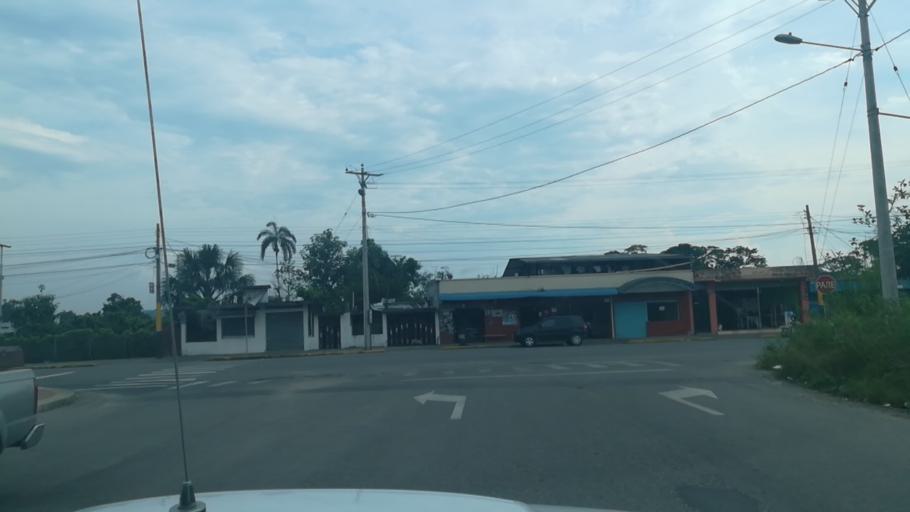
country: EC
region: Napo
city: Tena
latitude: -0.9858
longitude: -77.8245
